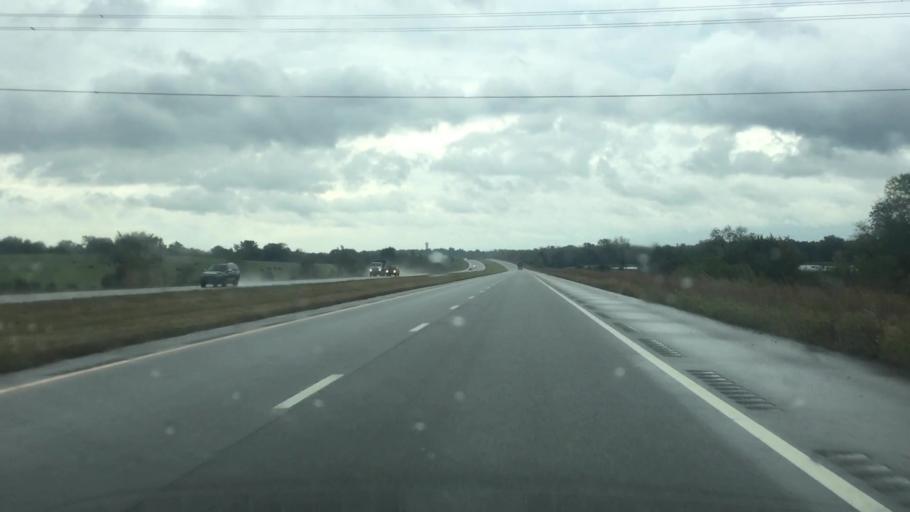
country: US
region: Kansas
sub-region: Miami County
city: Paola
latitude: 38.5432
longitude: -94.8809
